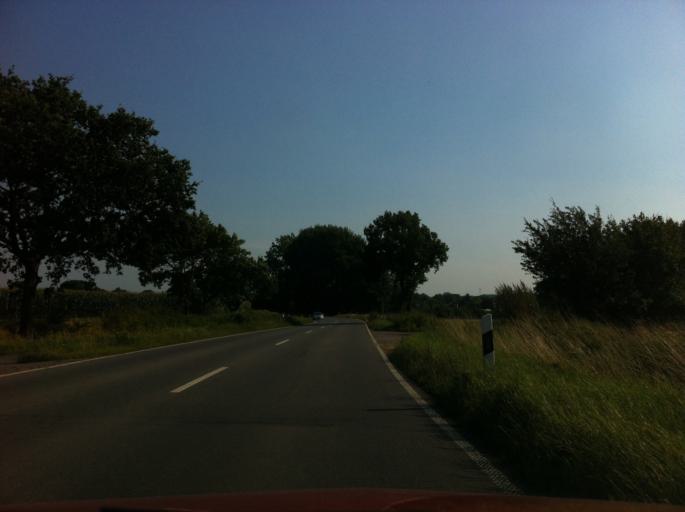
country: DE
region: Schleswig-Holstein
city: Harmsdorf
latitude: 54.3085
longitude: 10.8271
